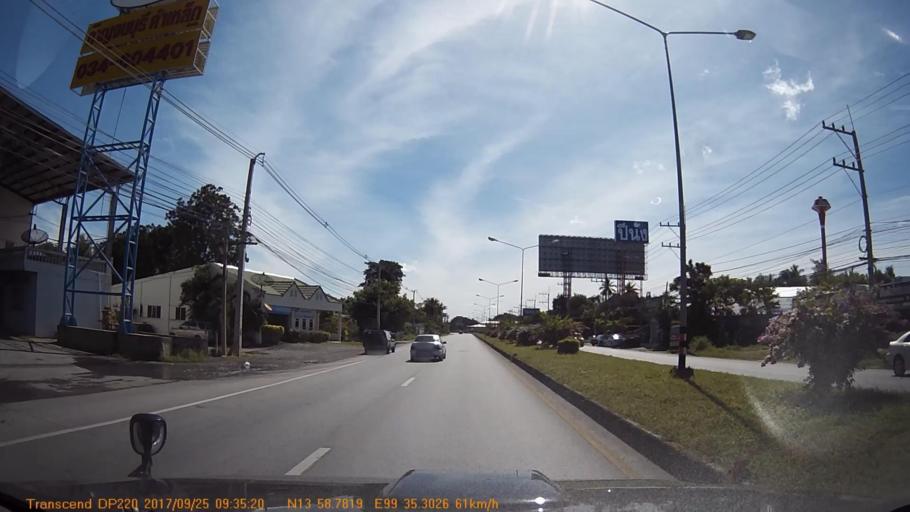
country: TH
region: Kanchanaburi
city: Kanchanaburi
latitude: 13.9797
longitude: 99.5884
